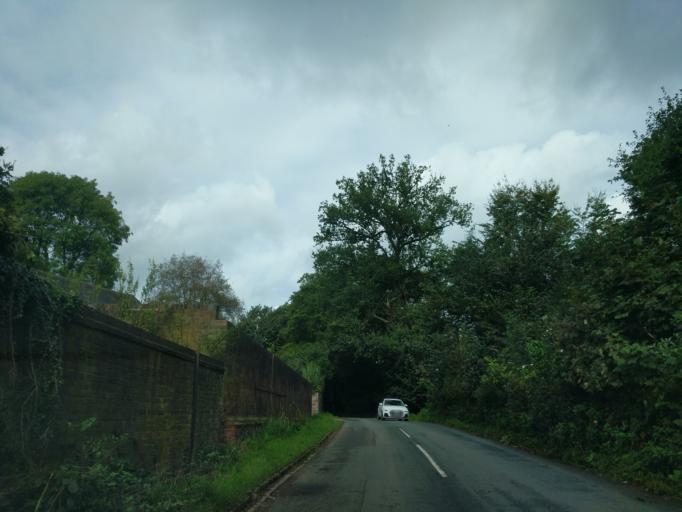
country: GB
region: England
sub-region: Staffordshire
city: Standon
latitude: 52.9707
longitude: -2.2841
